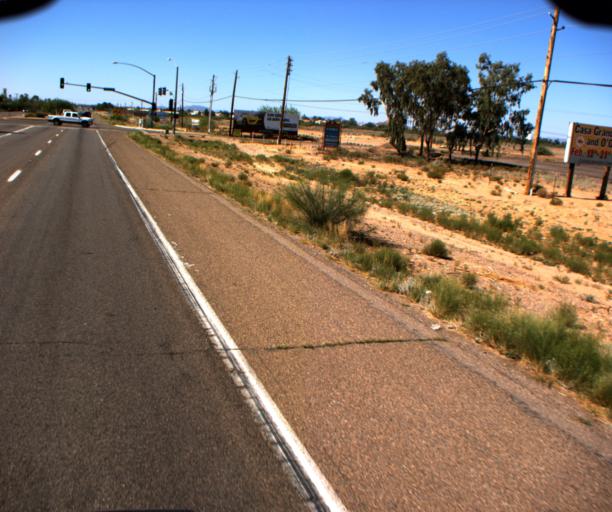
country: US
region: Arizona
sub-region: Pinal County
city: Casa Grande
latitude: 32.9243
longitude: -111.7570
